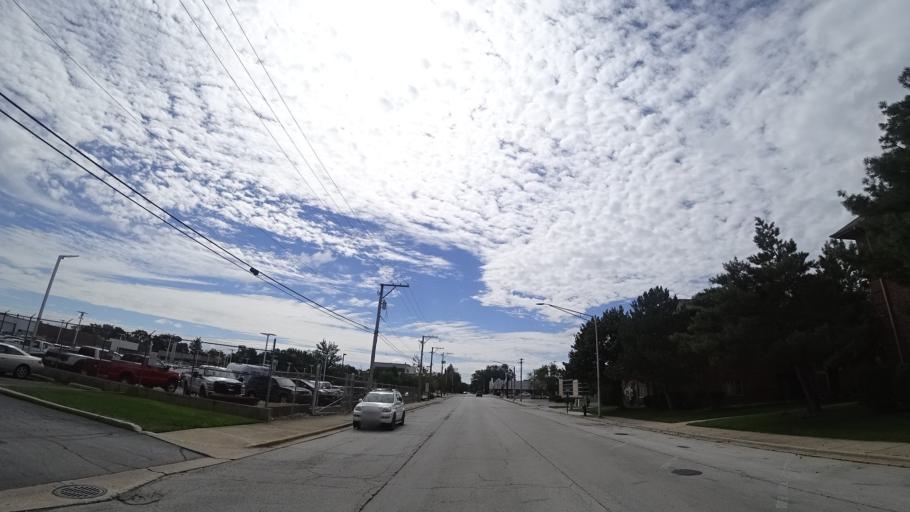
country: US
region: Illinois
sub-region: Cook County
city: Burbank
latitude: 41.7209
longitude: -87.7751
